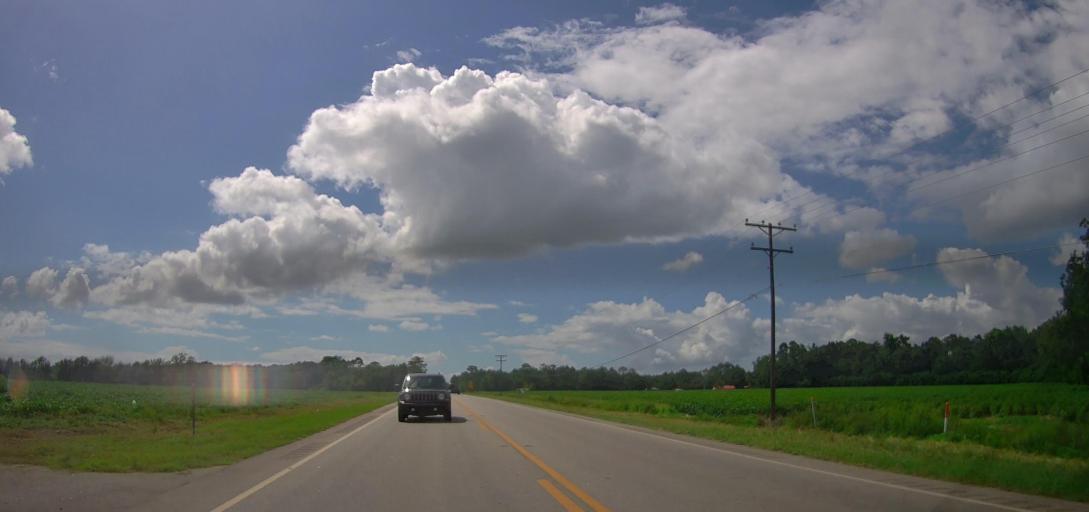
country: US
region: Georgia
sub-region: Coffee County
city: Broxton
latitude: 31.5533
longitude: -82.9600
